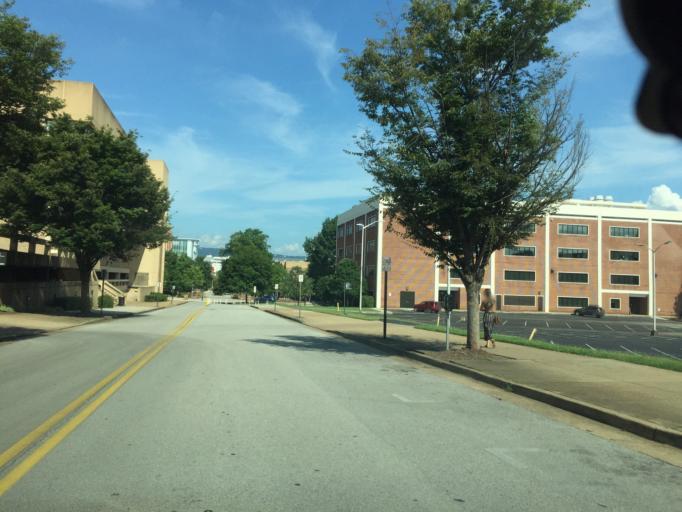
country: US
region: Tennessee
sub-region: Hamilton County
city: Chattanooga
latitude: 35.0464
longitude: -85.2963
